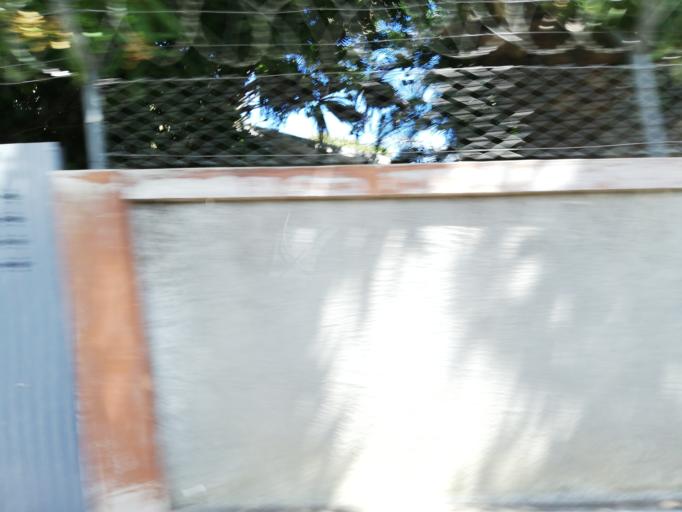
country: MU
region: Plaines Wilhems
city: Ebene
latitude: -20.2310
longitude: 57.4670
